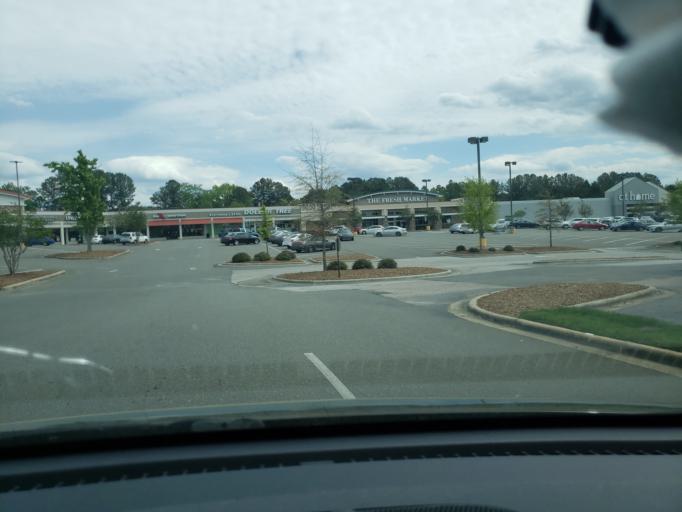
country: US
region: North Carolina
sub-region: Durham County
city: Durham
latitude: 35.9636
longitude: -78.9592
